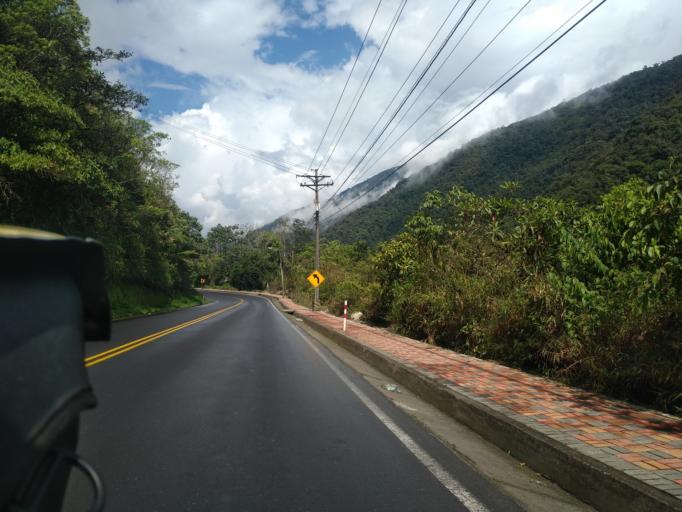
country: EC
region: Tungurahua
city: Banos
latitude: -1.4015
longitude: -78.2888
